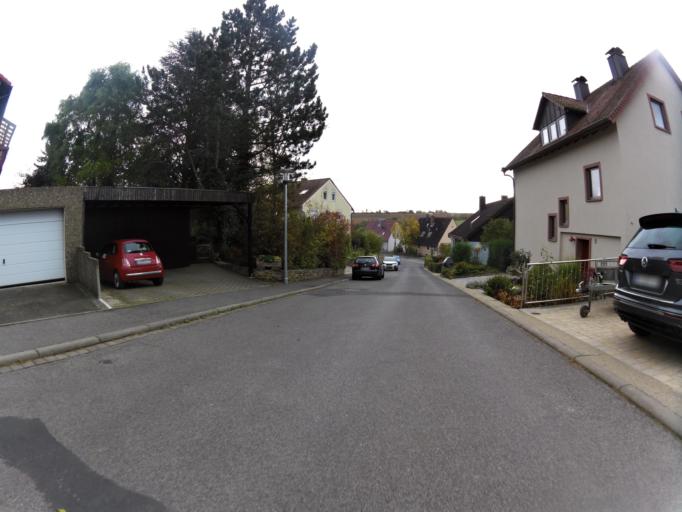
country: DE
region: Bavaria
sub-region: Regierungsbezirk Unterfranken
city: Kurnach
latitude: 49.8591
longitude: 10.0079
